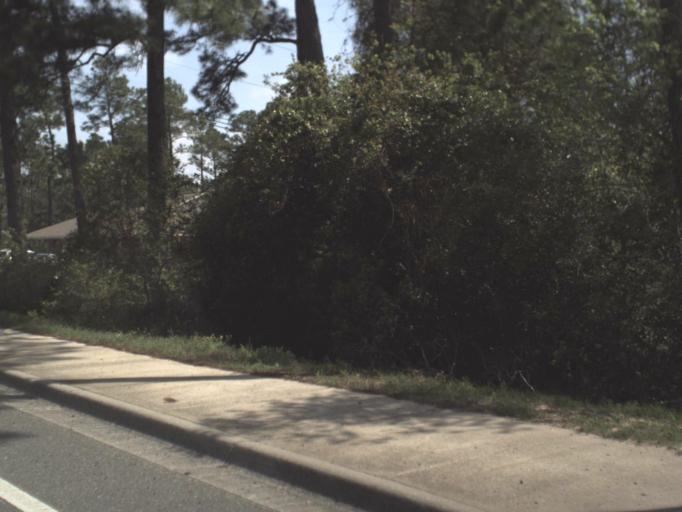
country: US
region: Florida
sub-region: Santa Rosa County
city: Navarre
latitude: 30.4141
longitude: -86.8693
